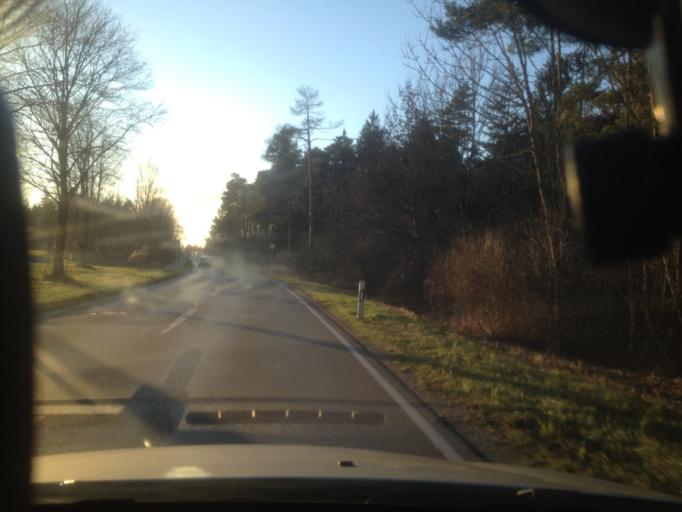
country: DE
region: Bavaria
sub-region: Swabia
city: Konigsbrunn
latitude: 48.2668
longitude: 10.9280
